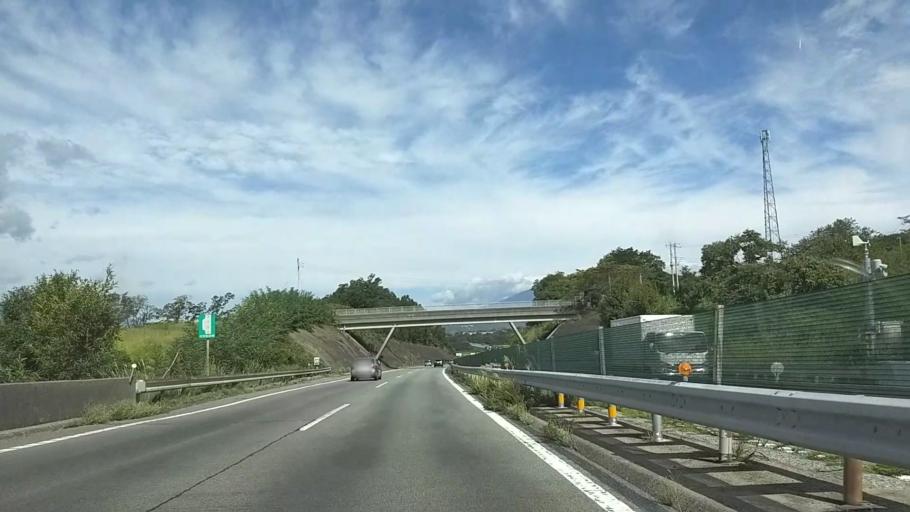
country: JP
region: Yamanashi
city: Nirasaki
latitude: 35.7327
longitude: 138.4547
